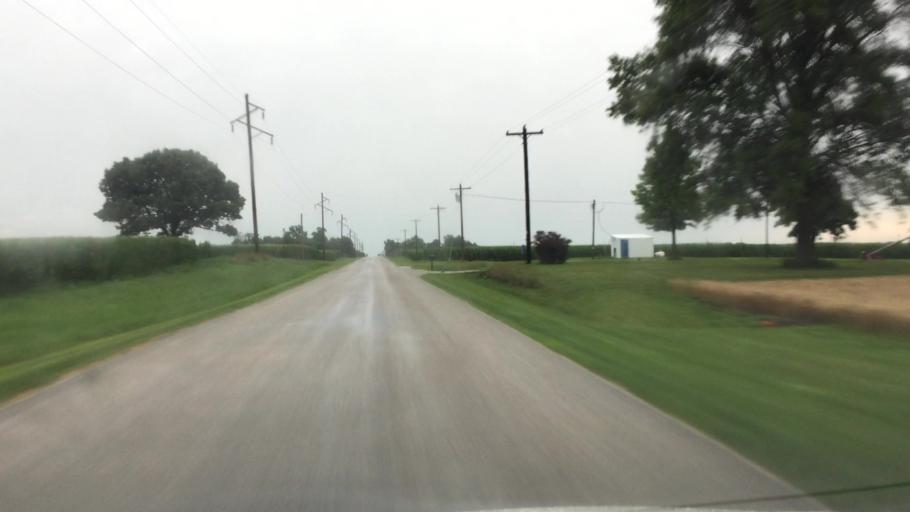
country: US
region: Illinois
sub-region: Hancock County
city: Hamilton
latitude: 40.4334
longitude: -91.2714
